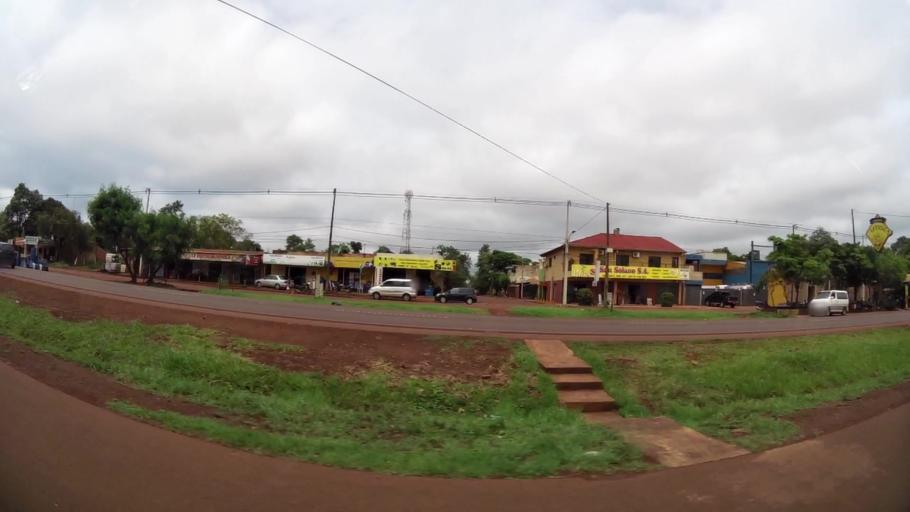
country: PY
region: Alto Parana
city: Ciudad del Este
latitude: -25.4923
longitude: -54.7346
